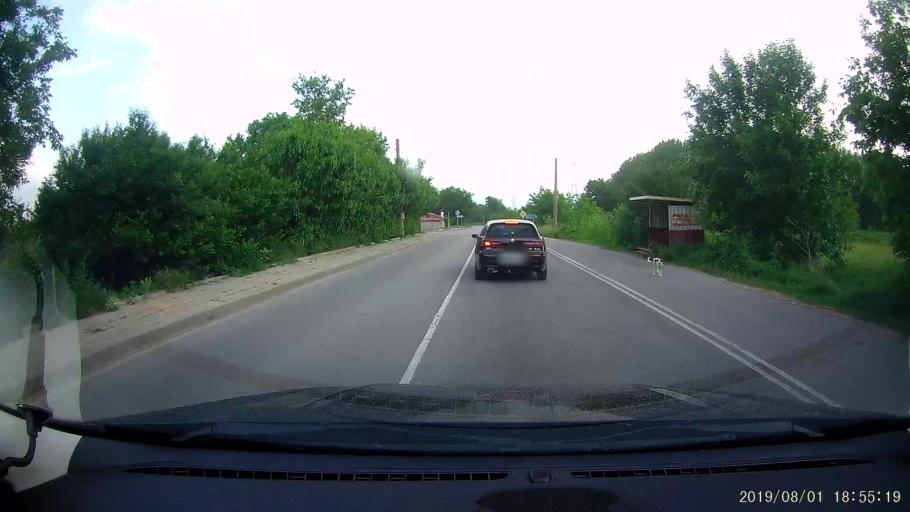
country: BG
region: Shumen
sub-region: Obshtina Smyadovo
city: Smyadovo
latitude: 43.1825
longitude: 27.0053
